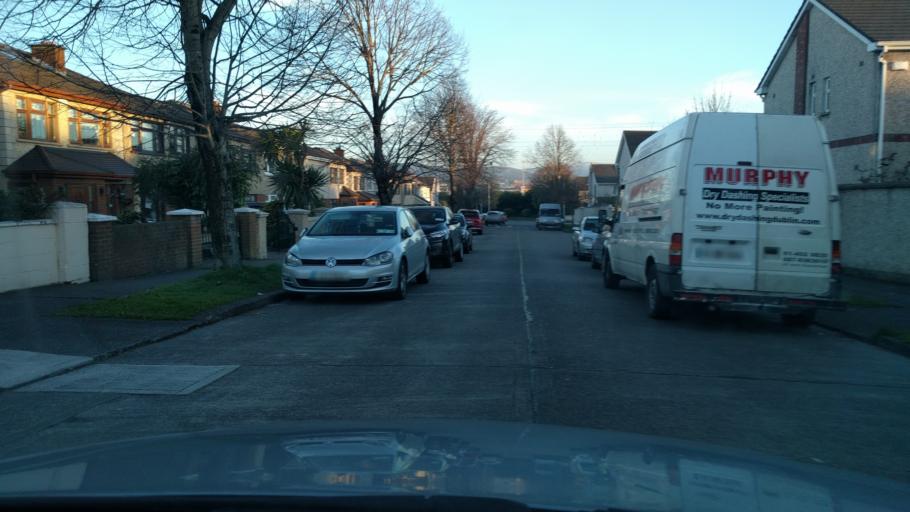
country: IE
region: Leinster
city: Tallaght
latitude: 53.2983
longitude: -6.3825
